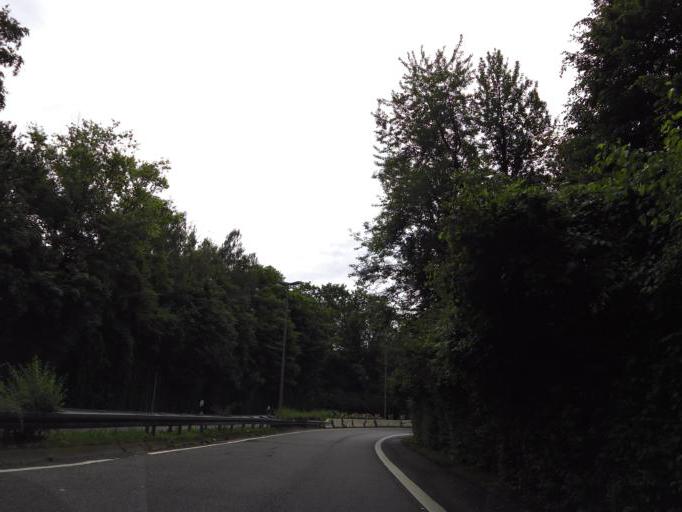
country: DE
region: Hesse
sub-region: Regierungsbezirk Darmstadt
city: Frankfurt am Main
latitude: 50.1555
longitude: 8.6384
